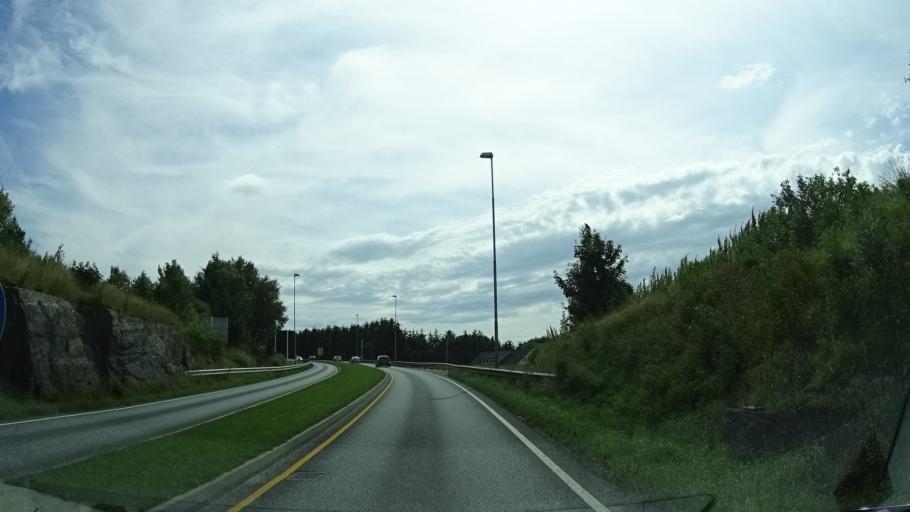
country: NO
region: Rogaland
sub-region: Randaberg
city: Randaberg
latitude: 58.9920
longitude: 5.6530
